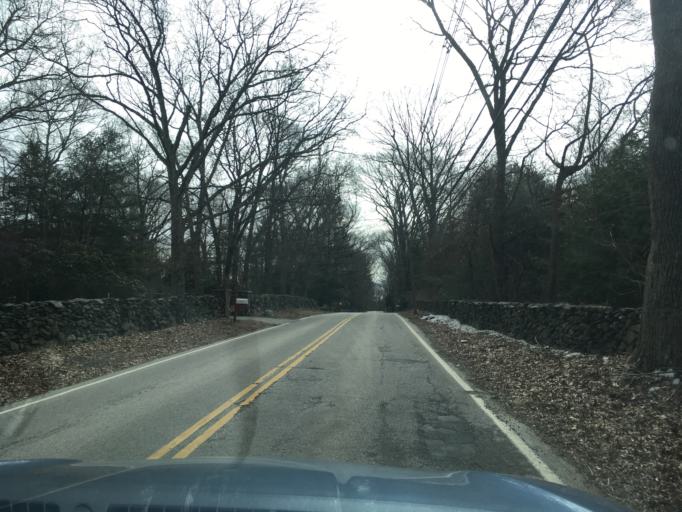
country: US
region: Rhode Island
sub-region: Kent County
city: East Greenwich
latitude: 41.6400
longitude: -71.4376
